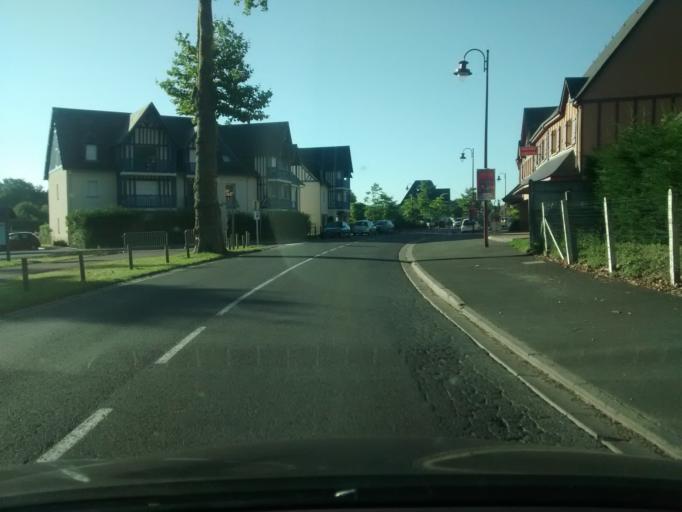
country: FR
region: Lower Normandy
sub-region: Departement du Calvados
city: Touques
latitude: 49.3397
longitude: 0.0914
